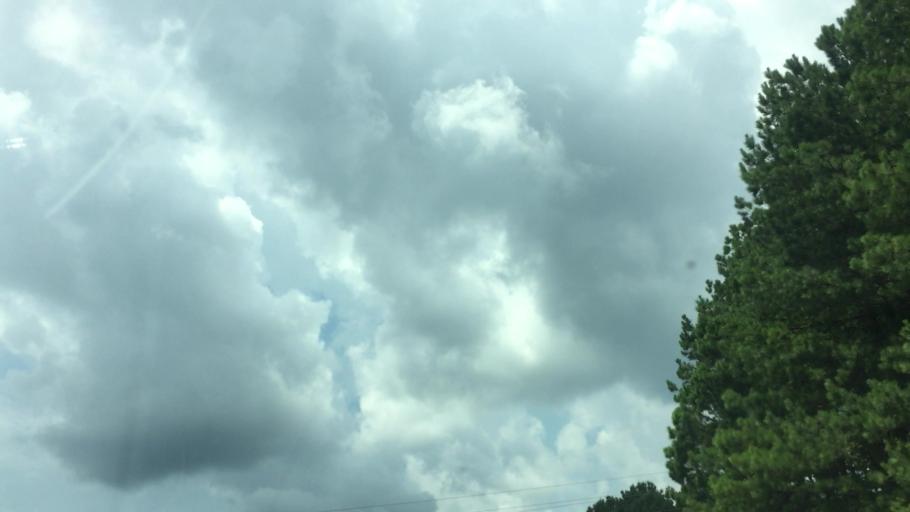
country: US
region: Georgia
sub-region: Fulton County
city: Palmetto
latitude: 33.5857
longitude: -84.6509
